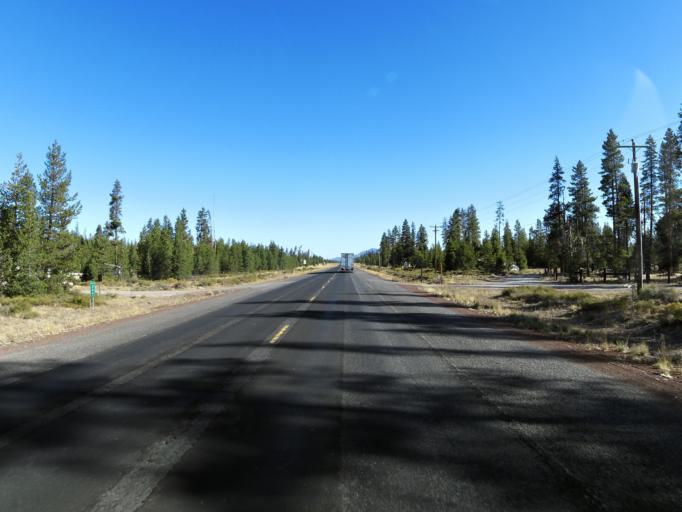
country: US
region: Oregon
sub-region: Deschutes County
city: La Pine
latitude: 43.1373
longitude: -121.8017
